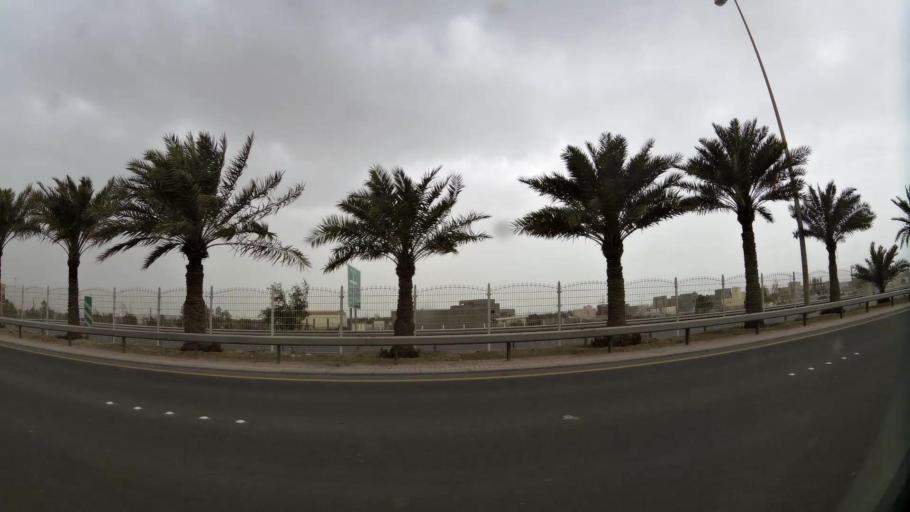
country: BH
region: Northern
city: Madinat `Isa
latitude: 26.1599
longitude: 50.5383
